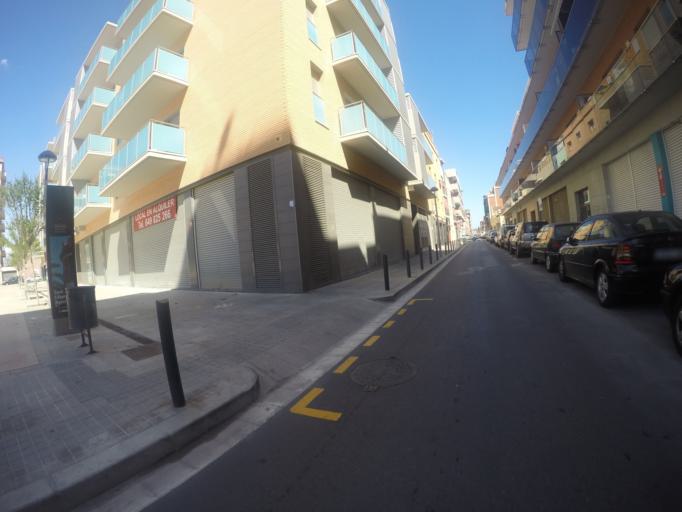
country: ES
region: Catalonia
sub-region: Provincia de Barcelona
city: Badalona
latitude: 41.4424
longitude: 2.2377
